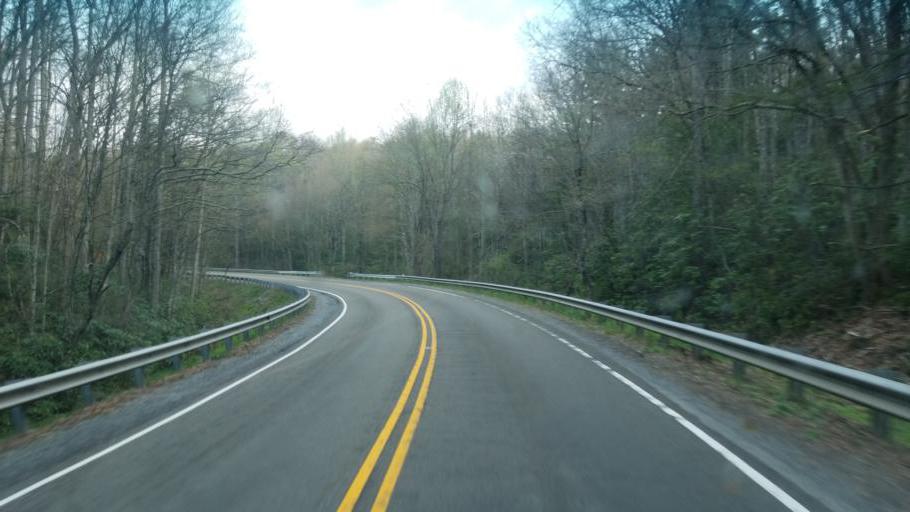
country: US
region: Virginia
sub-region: Smyth County
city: Atkins
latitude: 36.8089
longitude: -81.4040
